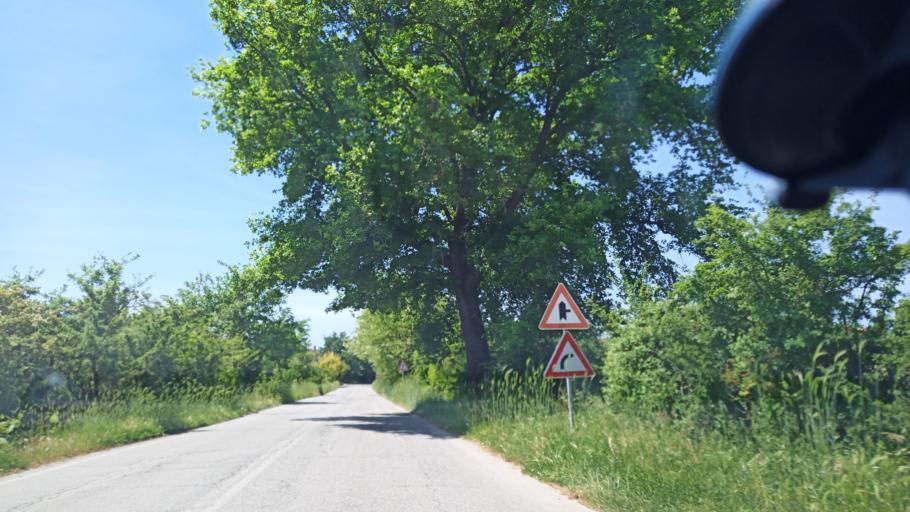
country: IT
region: Latium
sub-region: Provincia di Rieti
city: Forano
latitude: 42.3250
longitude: 12.5956
